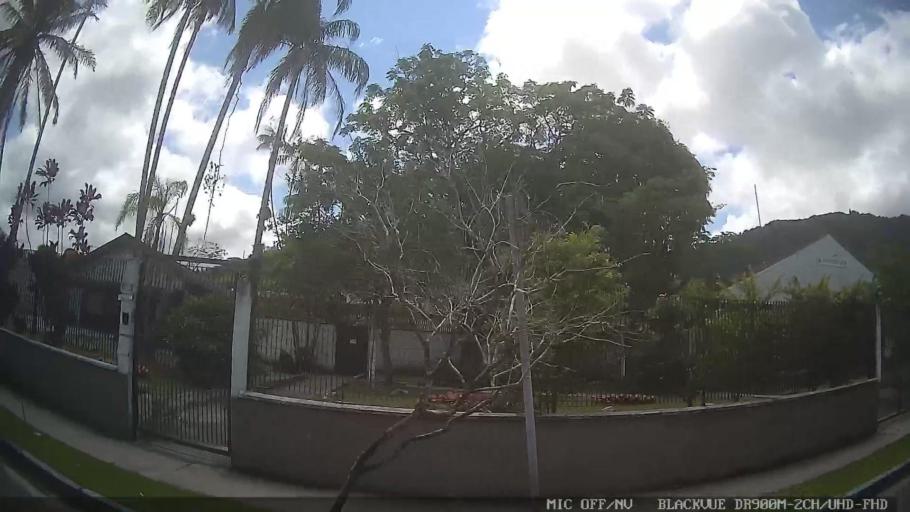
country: BR
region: Sao Paulo
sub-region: Caraguatatuba
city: Caraguatatuba
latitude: -23.6193
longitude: -45.4104
